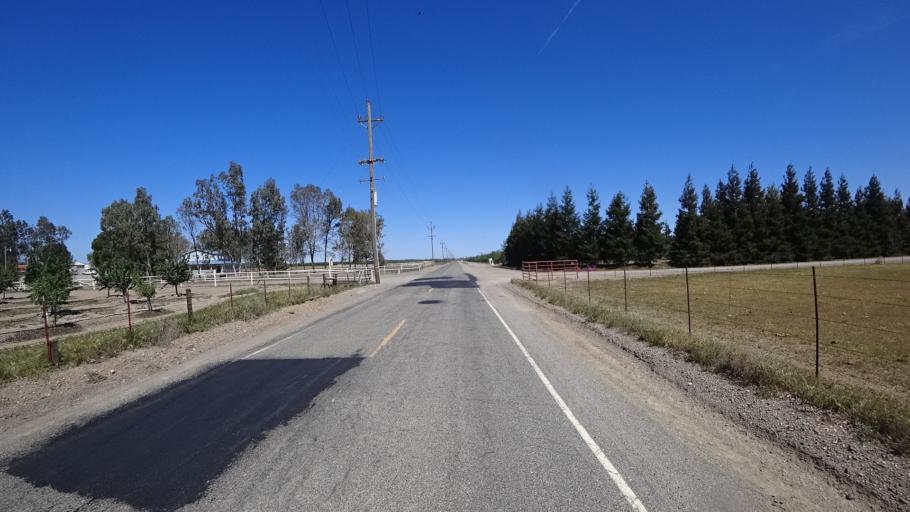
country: US
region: California
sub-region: Glenn County
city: Orland
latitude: 39.6674
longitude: -122.1783
